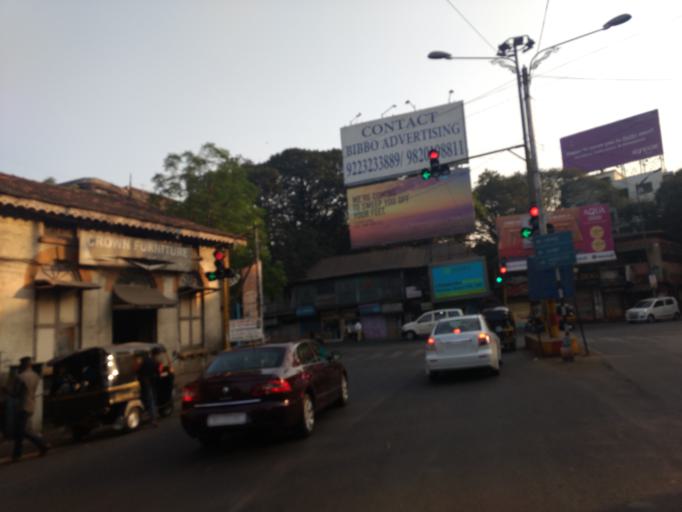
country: IN
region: Maharashtra
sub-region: Pune Division
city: Pune
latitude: 18.5073
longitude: 73.8793
